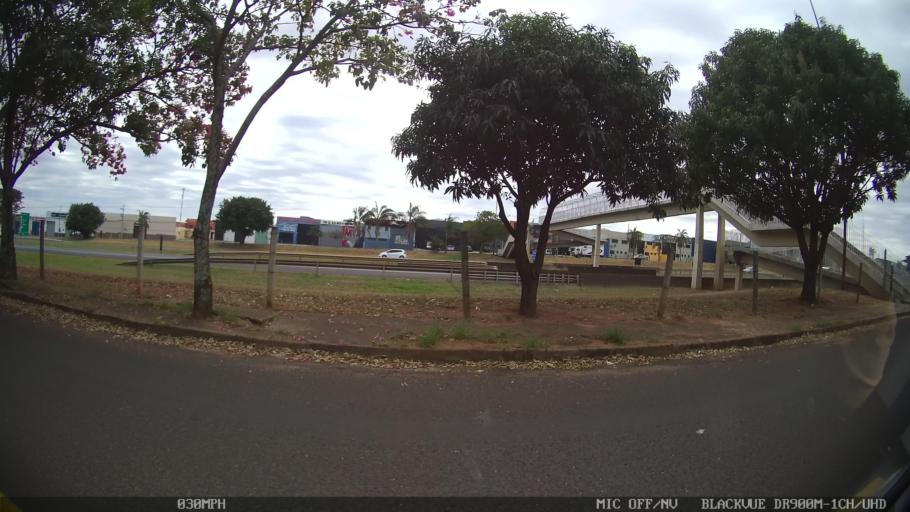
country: BR
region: Sao Paulo
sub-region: Sao Jose Do Rio Preto
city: Sao Jose do Rio Preto
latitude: -20.8103
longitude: -49.4965
